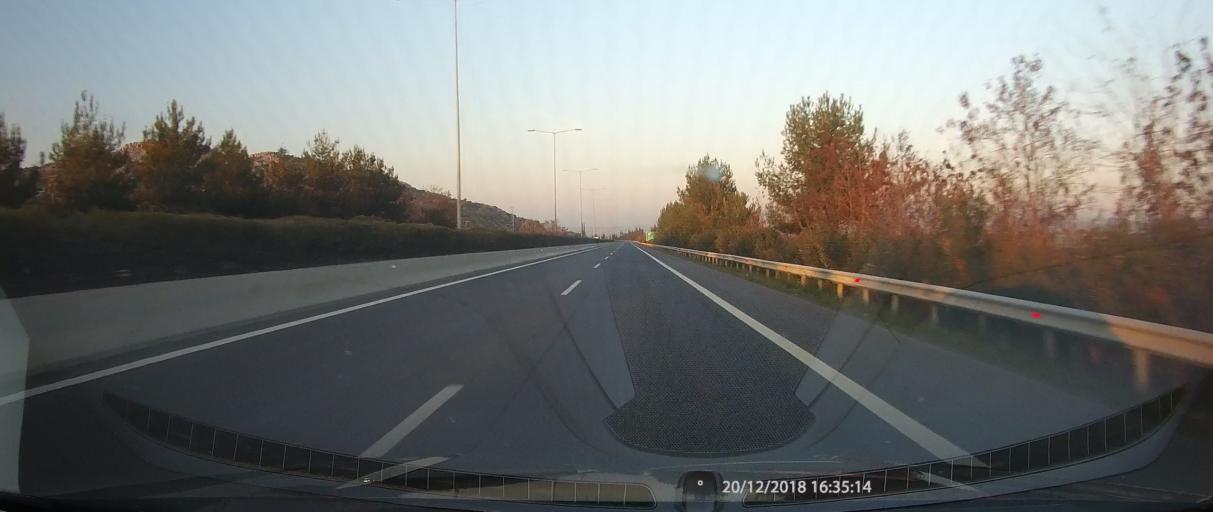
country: GR
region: Thessaly
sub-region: Nomos Magnisias
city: Nea Anchialos
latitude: 39.2993
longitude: 22.7462
